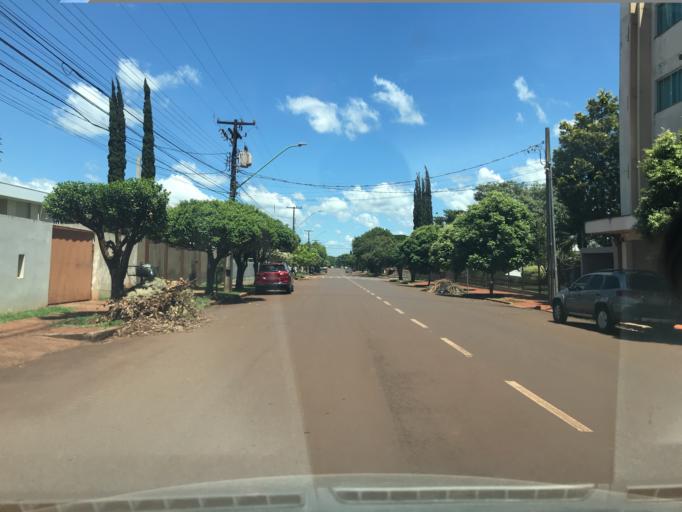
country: BR
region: Parana
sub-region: Palotina
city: Palotina
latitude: -24.2850
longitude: -53.8422
